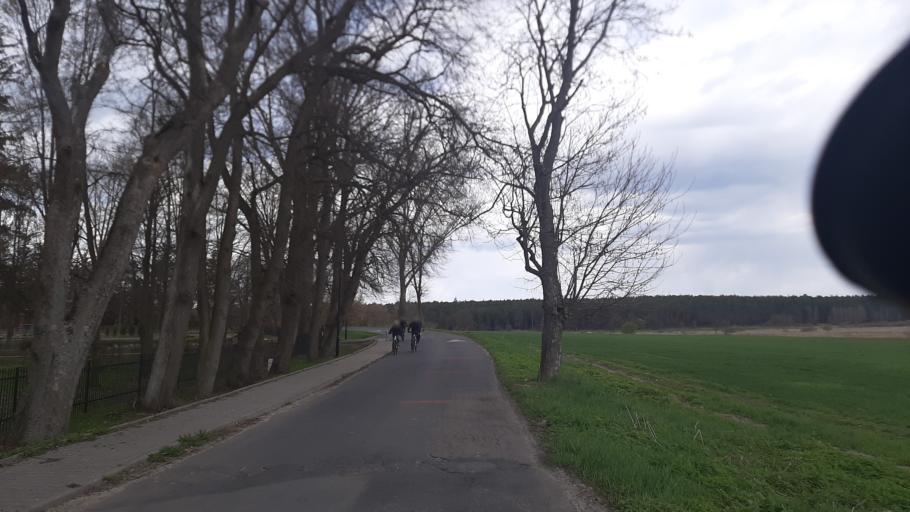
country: PL
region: Lublin Voivodeship
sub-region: Powiat lubelski
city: Niemce
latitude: 51.3631
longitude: 22.5542
